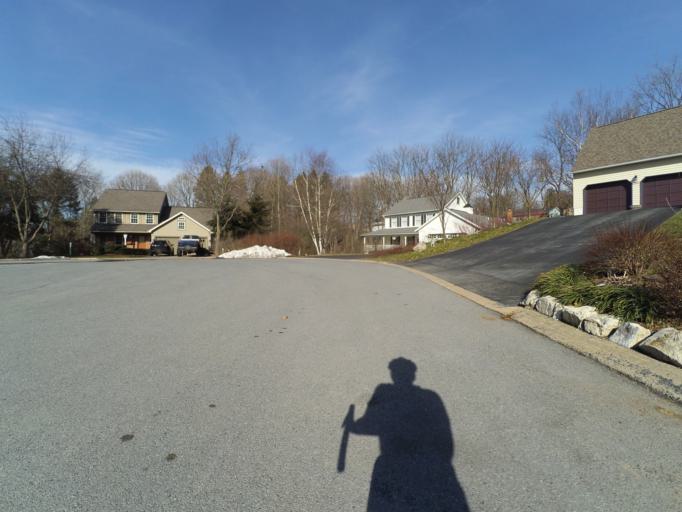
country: US
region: Pennsylvania
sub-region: Centre County
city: Lemont
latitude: 40.8138
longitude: -77.8178
